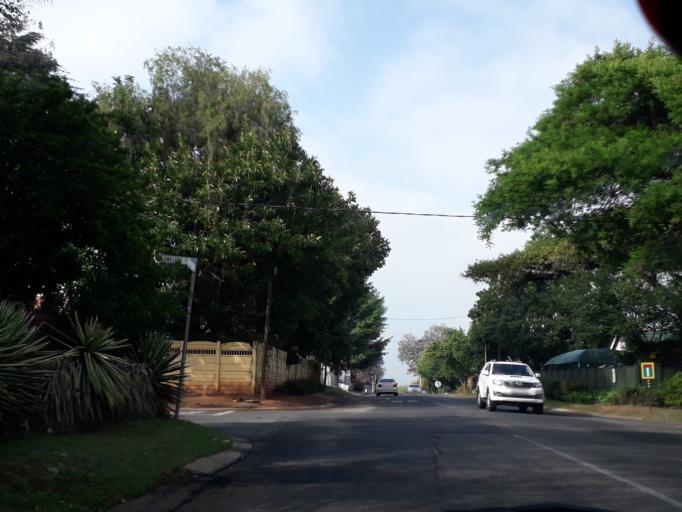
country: ZA
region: Gauteng
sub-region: City of Johannesburg Metropolitan Municipality
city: Johannesburg
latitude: -26.0935
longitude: 28.0385
